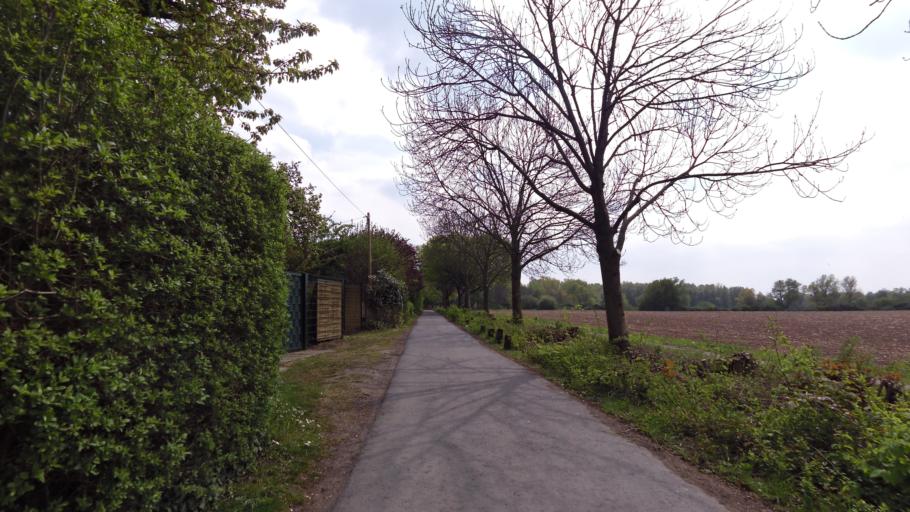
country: DE
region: Lower Saxony
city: Hemmingen
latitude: 52.3315
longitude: 9.7474
